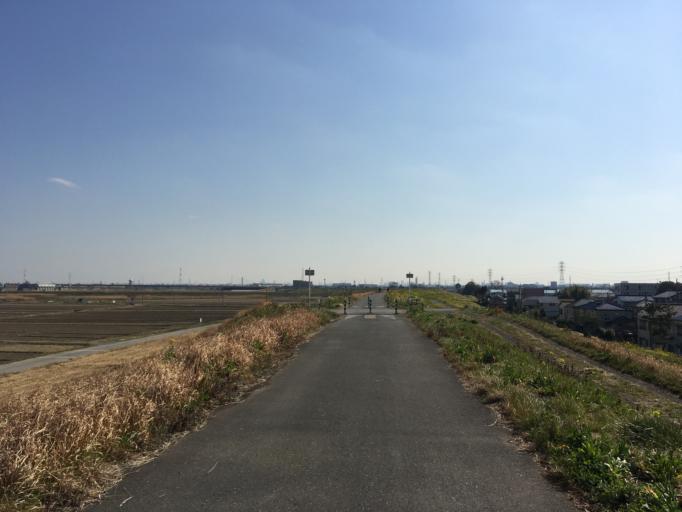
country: JP
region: Saitama
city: Shiki
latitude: 35.8463
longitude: 139.5913
